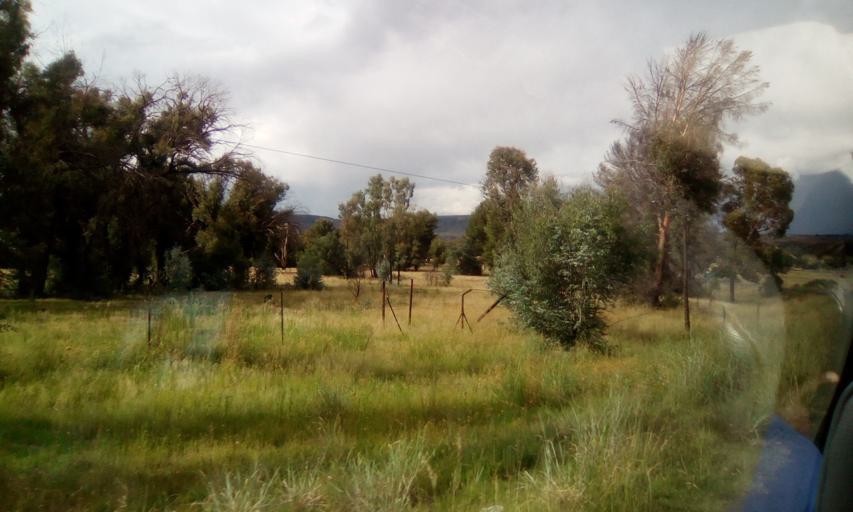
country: ZA
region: Orange Free State
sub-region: Thabo Mofutsanyana District Municipality
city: Ladybrand
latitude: -29.2111
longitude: 27.4661
